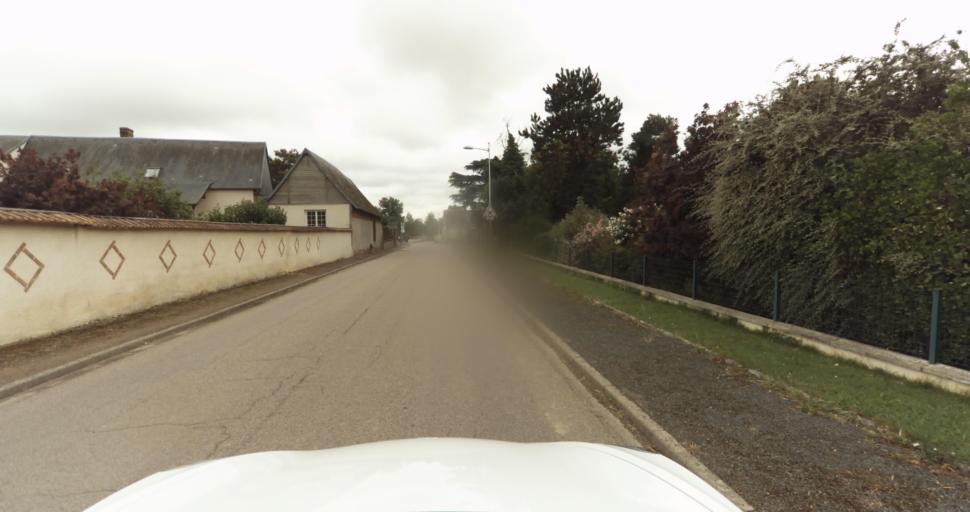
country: FR
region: Haute-Normandie
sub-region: Departement de l'Eure
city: Aviron
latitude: 49.0545
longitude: 1.0865
